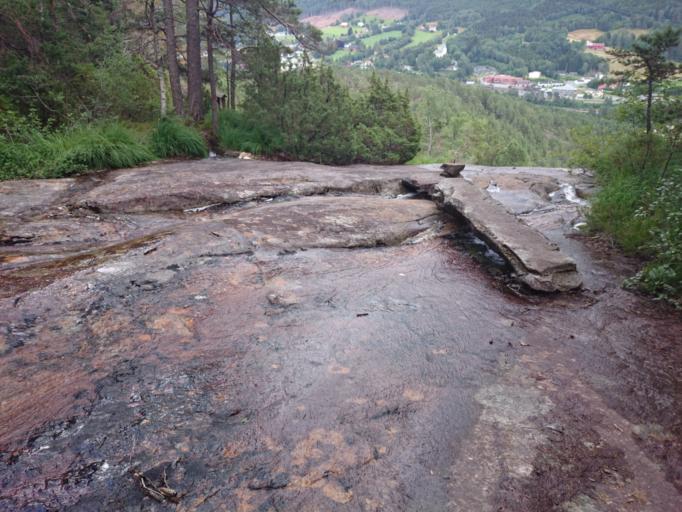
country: NO
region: Aust-Agder
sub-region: Amli
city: Amli
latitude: 58.7691
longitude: 8.4664
